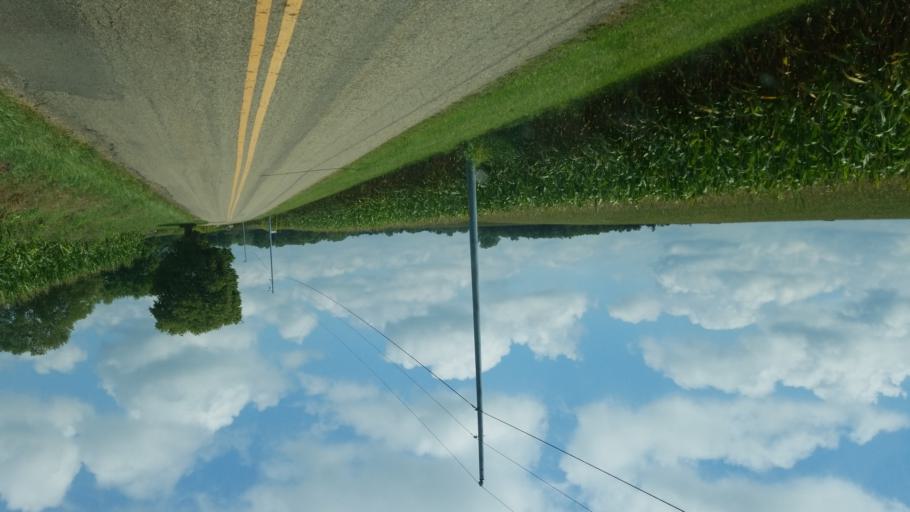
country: US
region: Ohio
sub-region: Licking County
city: Utica
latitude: 40.2668
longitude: -82.4825
